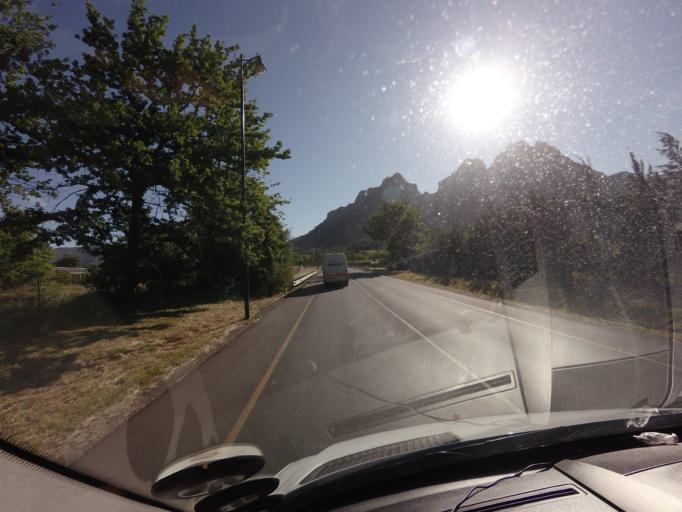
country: ZA
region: Western Cape
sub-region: Cape Winelands District Municipality
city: Stellenbosch
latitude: -33.8896
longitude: 18.9624
